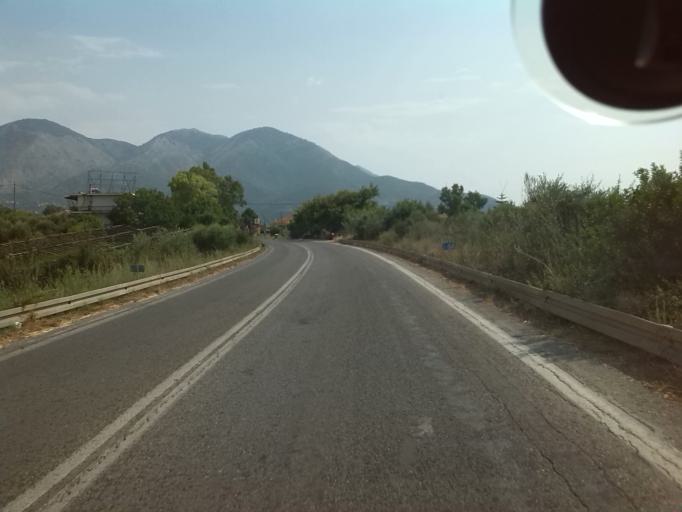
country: GR
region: Peloponnese
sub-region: Nomos Messinias
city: Kyparissia
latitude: 37.2791
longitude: 21.6985
